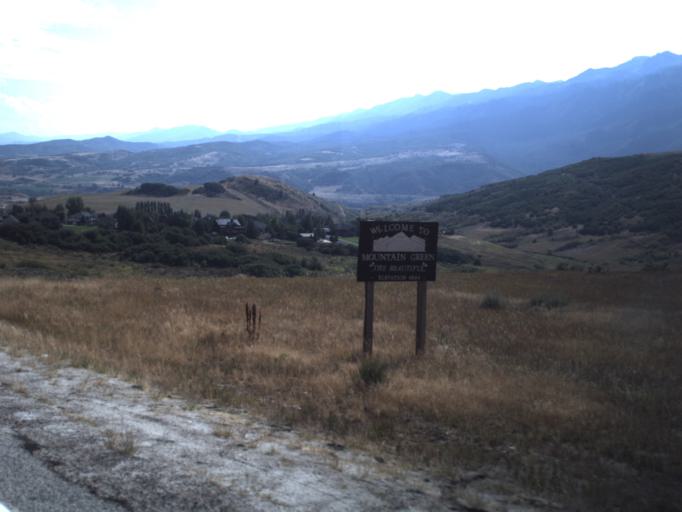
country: US
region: Utah
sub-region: Morgan County
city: Mountain Green
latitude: 41.1670
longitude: -111.8012
